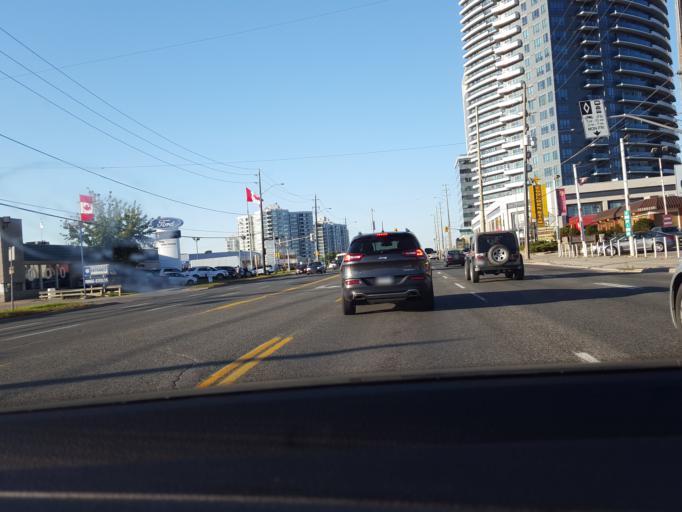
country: CA
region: Ontario
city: North York
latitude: 43.8007
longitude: -79.4207
